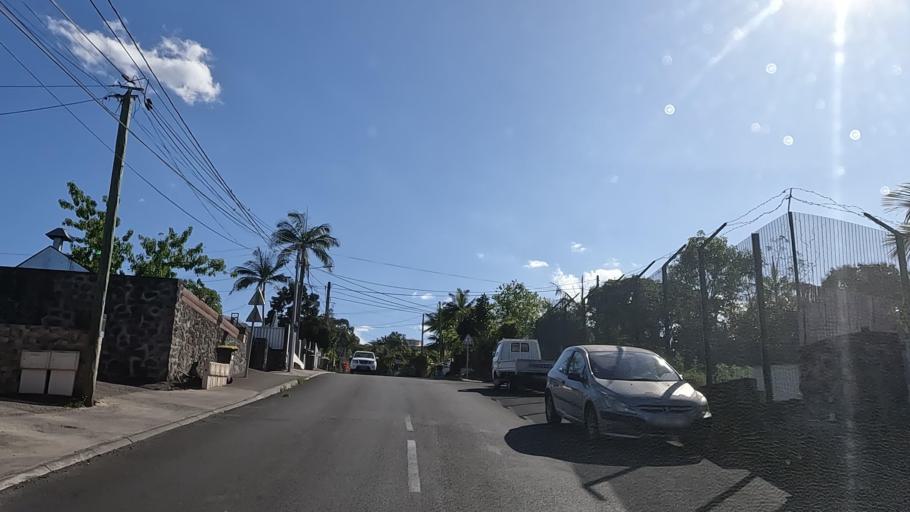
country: RE
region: Reunion
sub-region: Reunion
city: Le Tampon
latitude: -21.2586
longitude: 55.5132
